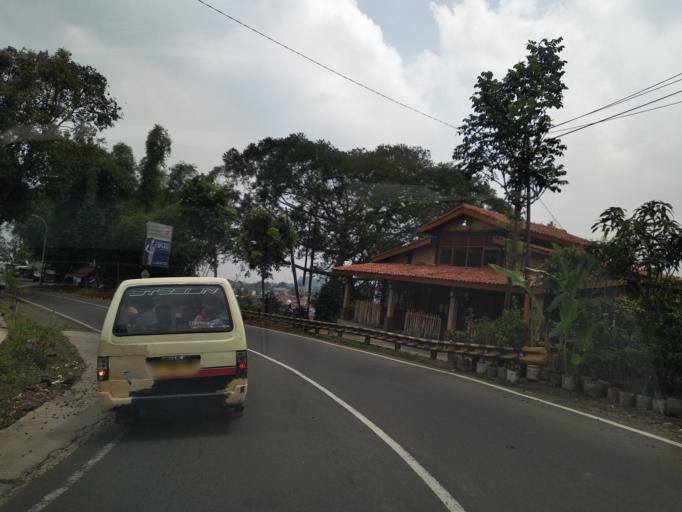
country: ID
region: West Java
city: Lembang
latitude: -6.8360
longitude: 107.6000
